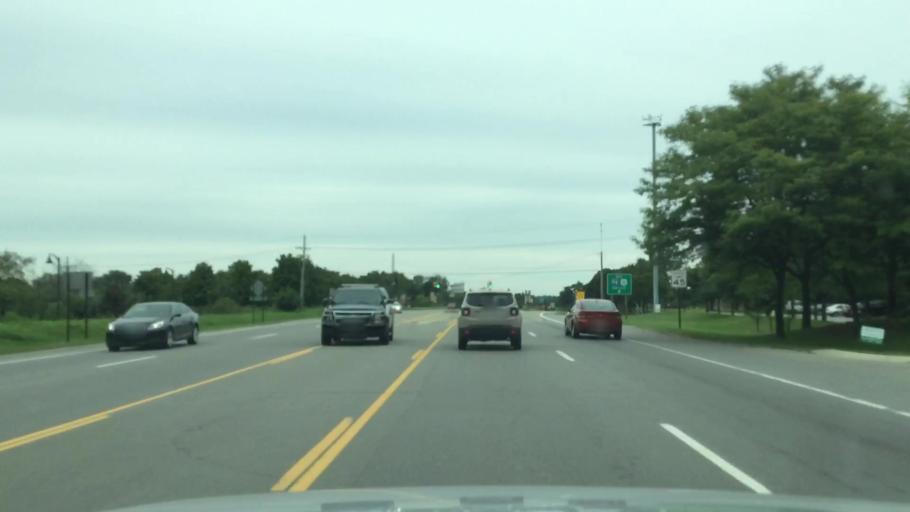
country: US
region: Michigan
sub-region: Washtenaw County
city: Ypsilanti
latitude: 42.2254
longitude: -83.6176
